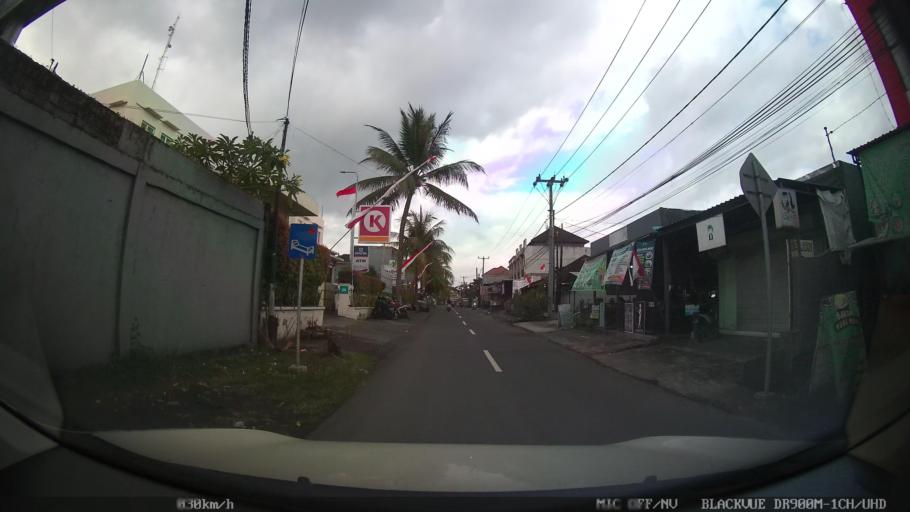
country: ID
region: Bali
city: Banjar Tegal Belodan
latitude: -8.5473
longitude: 115.1199
